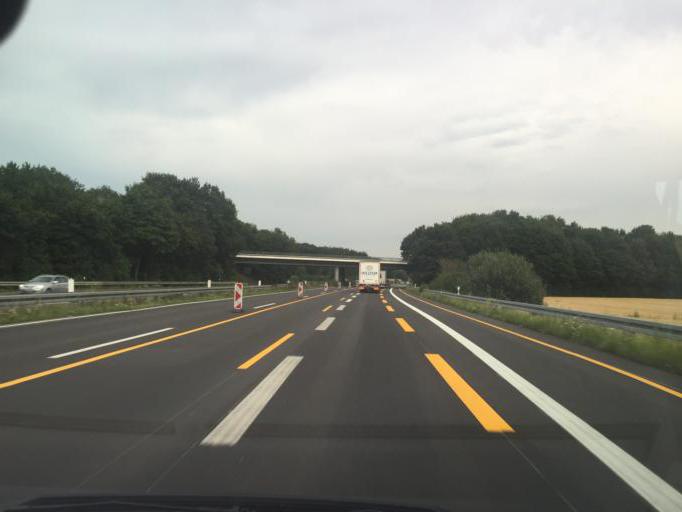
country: DE
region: North Rhine-Westphalia
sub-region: Regierungsbezirk Dusseldorf
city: Viersen
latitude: 51.2738
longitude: 6.3476
